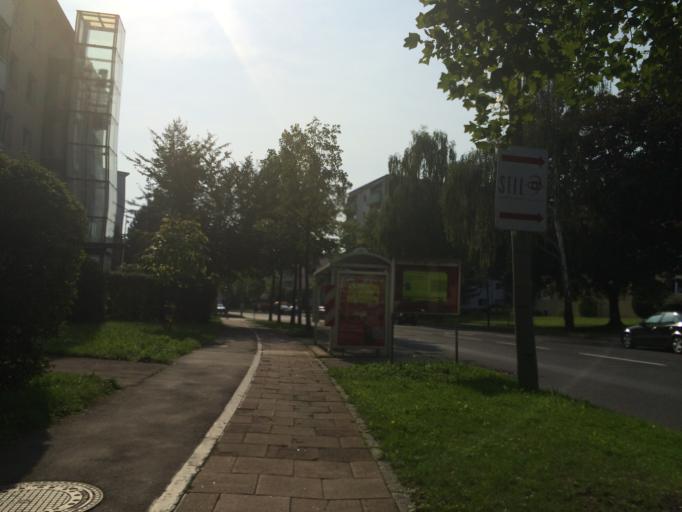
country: AT
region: Upper Austria
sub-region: Linz Stadt
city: Linz
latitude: 48.2765
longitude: 14.3016
